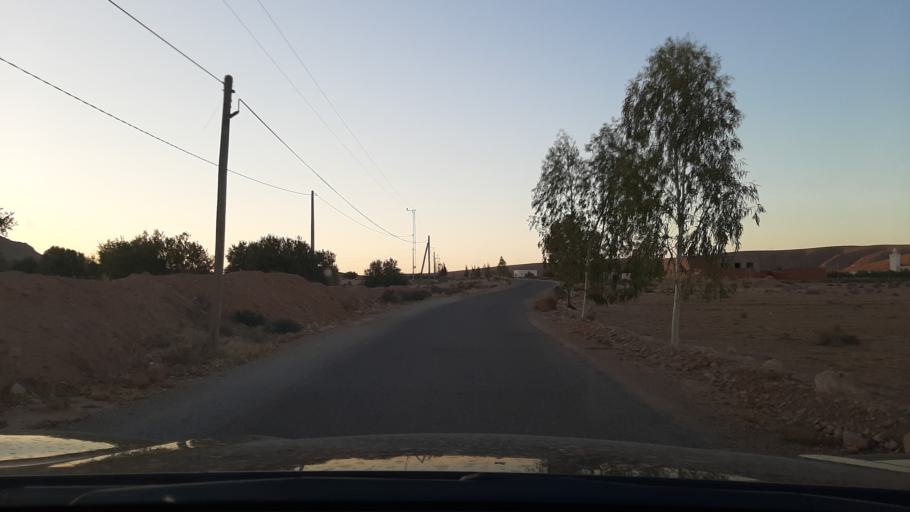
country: TN
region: Qabis
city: Matmata
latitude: 33.5664
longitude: 10.1783
